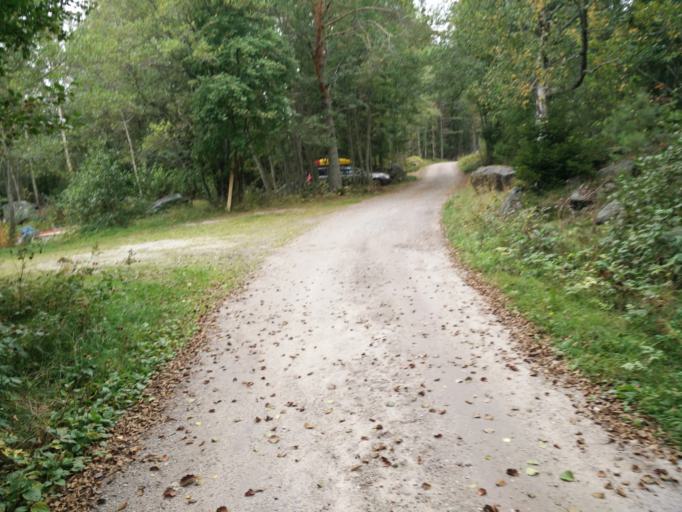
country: SE
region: Gaevleborg
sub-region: Hudiksvalls Kommun
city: Hudiksvall
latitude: 61.8332
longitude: 17.3388
